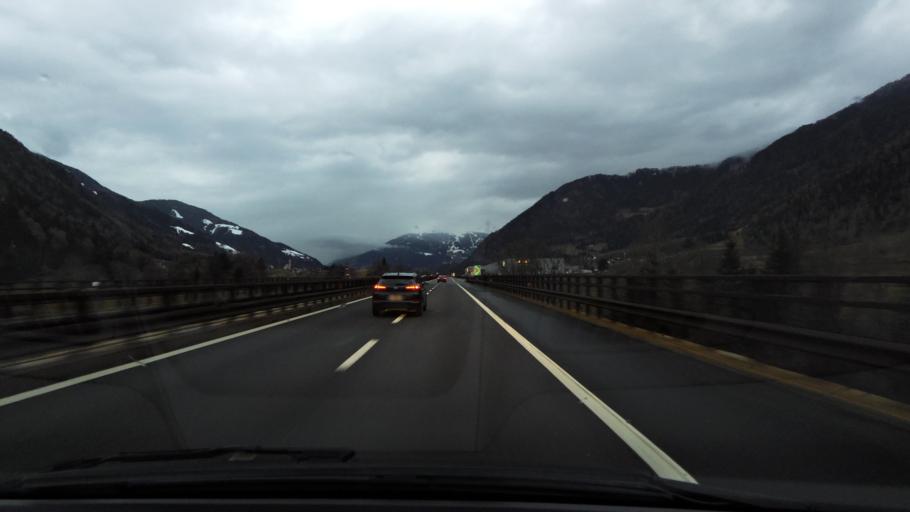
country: IT
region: Trentino-Alto Adige
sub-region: Bolzano
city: Campo di Trens
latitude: 46.8631
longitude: 11.4983
